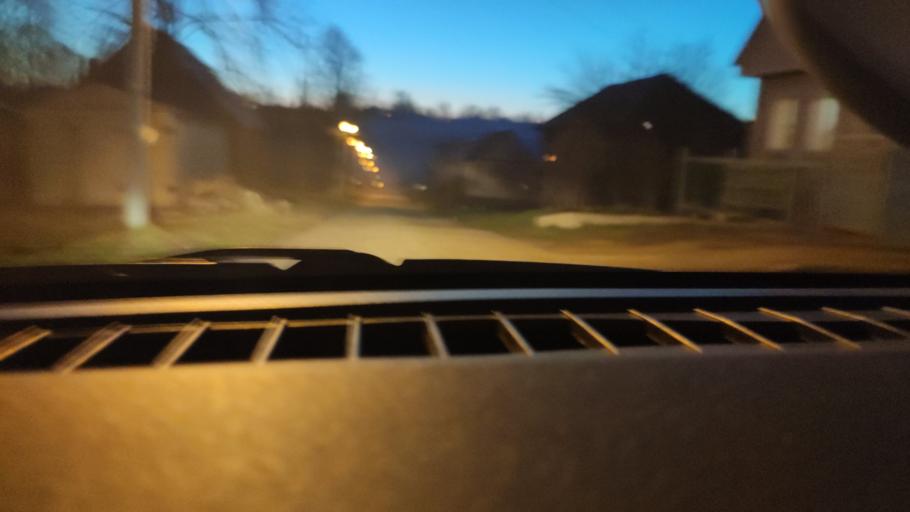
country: RU
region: Perm
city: Perm
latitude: 58.0410
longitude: 56.3344
